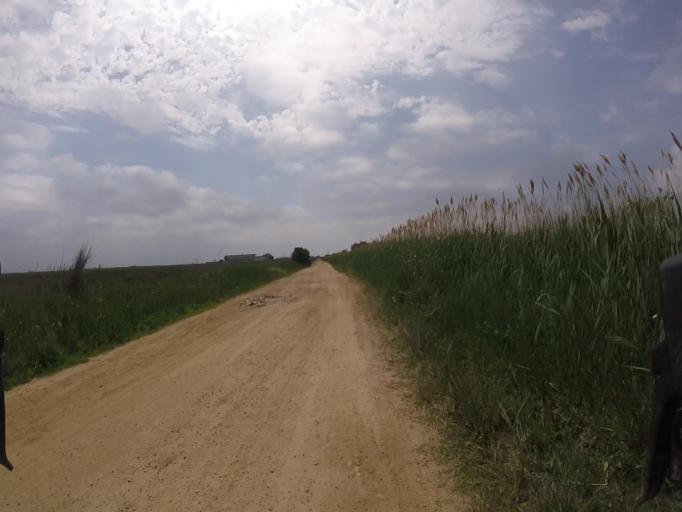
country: ES
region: Valencia
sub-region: Provincia de Castello
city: Orpesa/Oropesa del Mar
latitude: 40.1419
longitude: 0.1639
